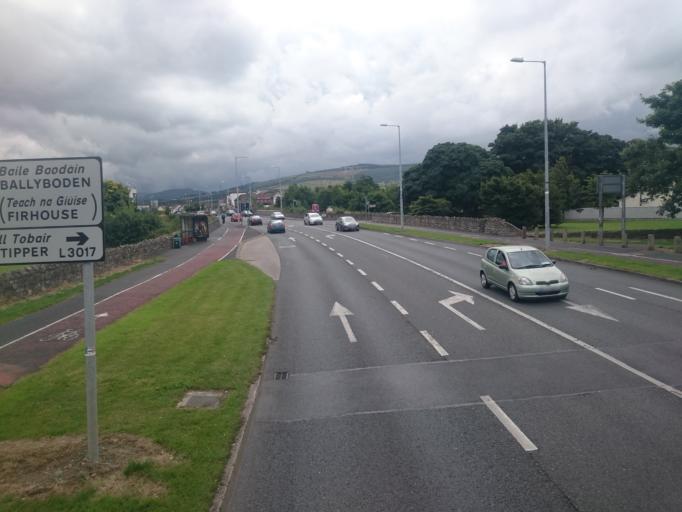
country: IE
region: Leinster
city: Oldbawn
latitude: 53.2768
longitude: -6.3568
